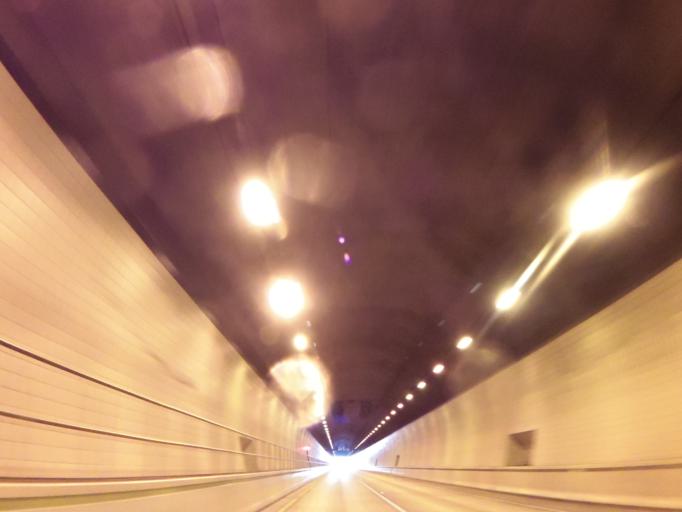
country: US
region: Tennessee
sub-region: Claiborne County
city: Harrogate
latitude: 36.6004
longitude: -83.6802
